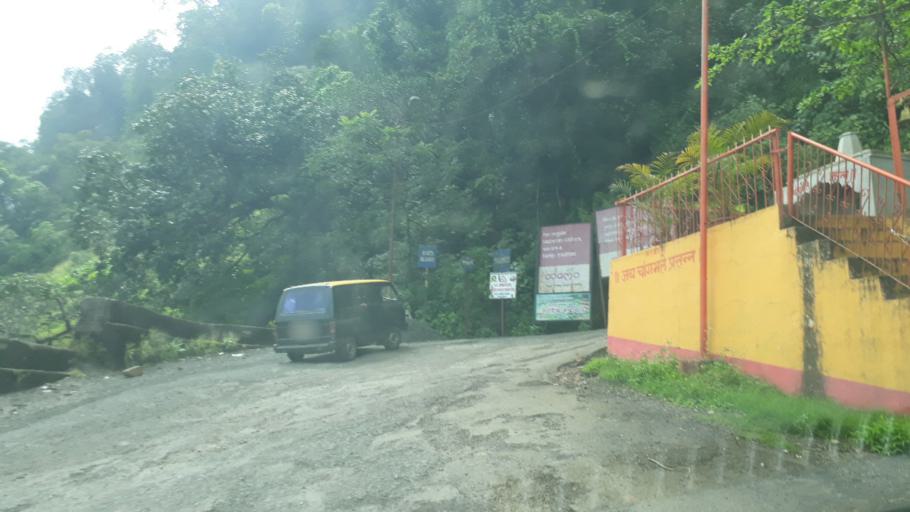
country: IN
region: Maharashtra
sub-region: Raigarh
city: Matheran
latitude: 19.0013
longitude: 73.2853
